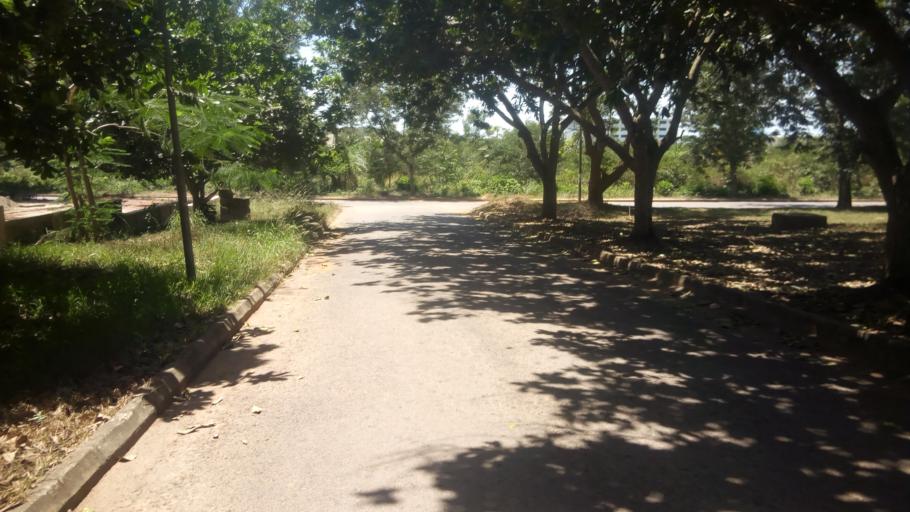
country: GH
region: Central
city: Cape Coast
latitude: 5.1216
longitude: -1.2911
